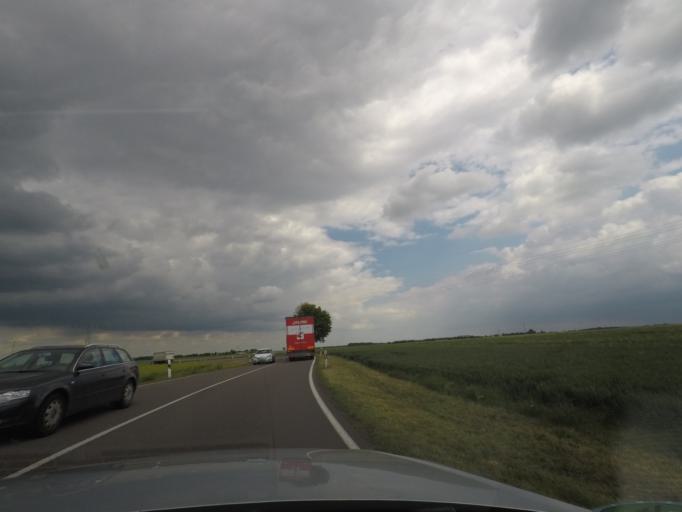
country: DE
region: Saxony-Anhalt
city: Gunthersdorf
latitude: 51.3371
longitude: 12.2074
